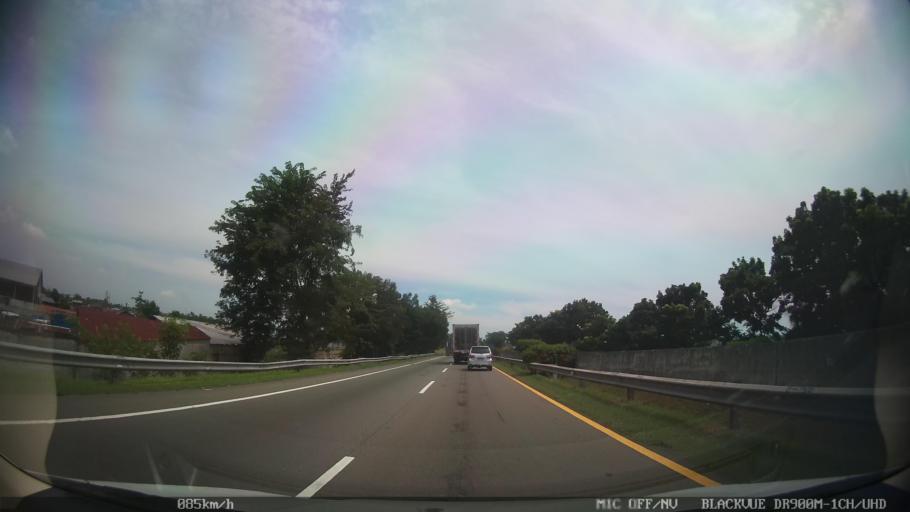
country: ID
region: North Sumatra
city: Labuhan Deli
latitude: 3.6904
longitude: 98.6821
